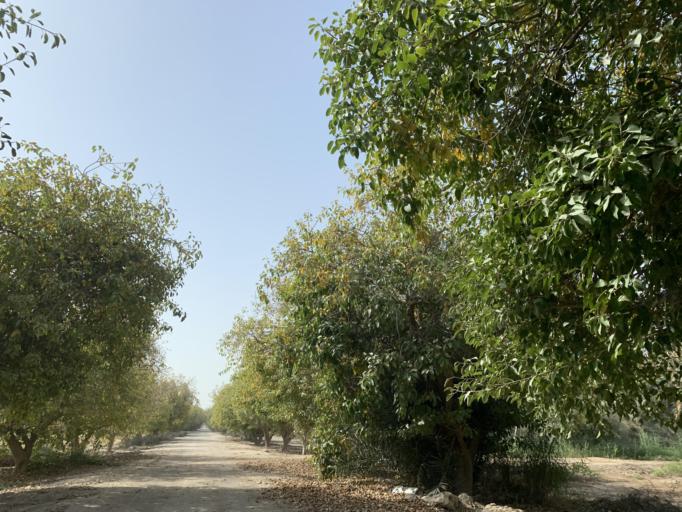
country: BH
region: Northern
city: Madinat `Isa
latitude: 26.1677
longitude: 50.5294
